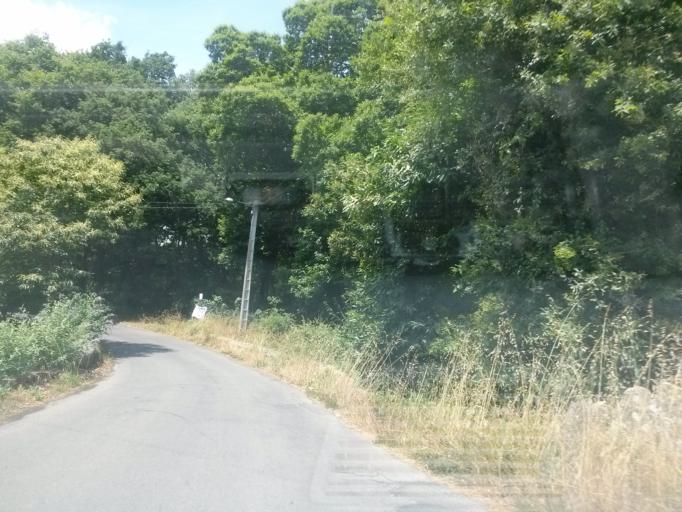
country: ES
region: Galicia
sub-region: Provincia de Lugo
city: Lugo
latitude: 43.0364
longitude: -7.5909
